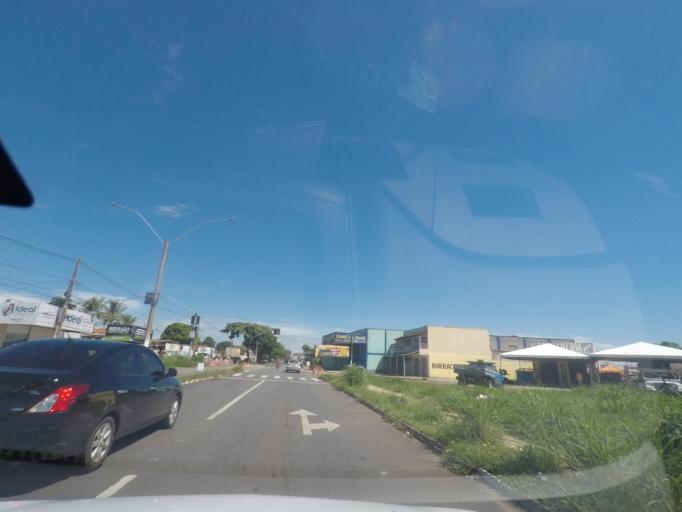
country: BR
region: Goias
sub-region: Aparecida De Goiania
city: Aparecida de Goiania
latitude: -16.7741
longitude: -49.3386
